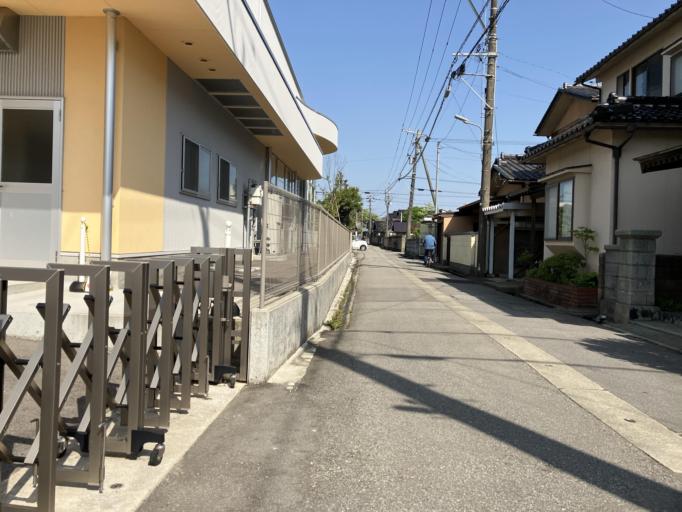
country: JP
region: Toyama
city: Takaoka
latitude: 36.7445
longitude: 137.0244
